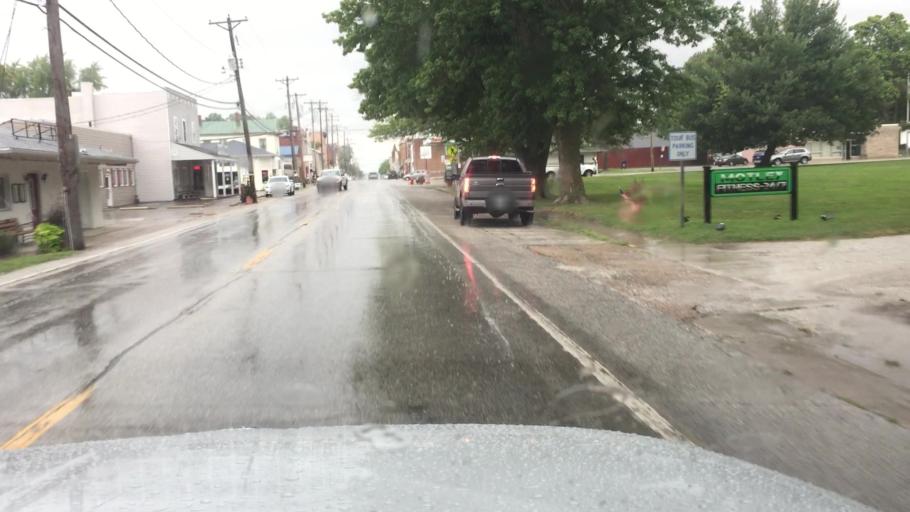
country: US
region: Illinois
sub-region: Hancock County
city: Nauvoo
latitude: 40.5497
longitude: -91.3792
